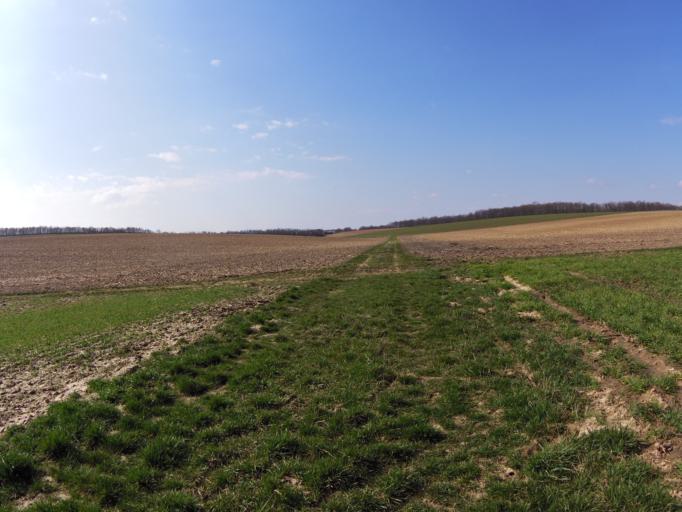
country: DE
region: Bavaria
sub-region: Regierungsbezirk Unterfranken
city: Rottendorf
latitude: 49.7999
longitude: 10.0647
